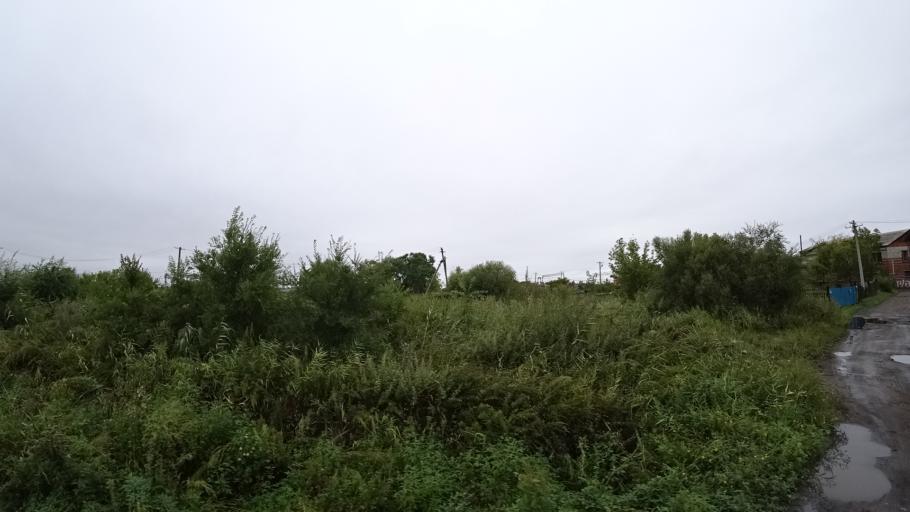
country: RU
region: Primorskiy
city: Monastyrishche
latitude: 44.2116
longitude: 132.4443
